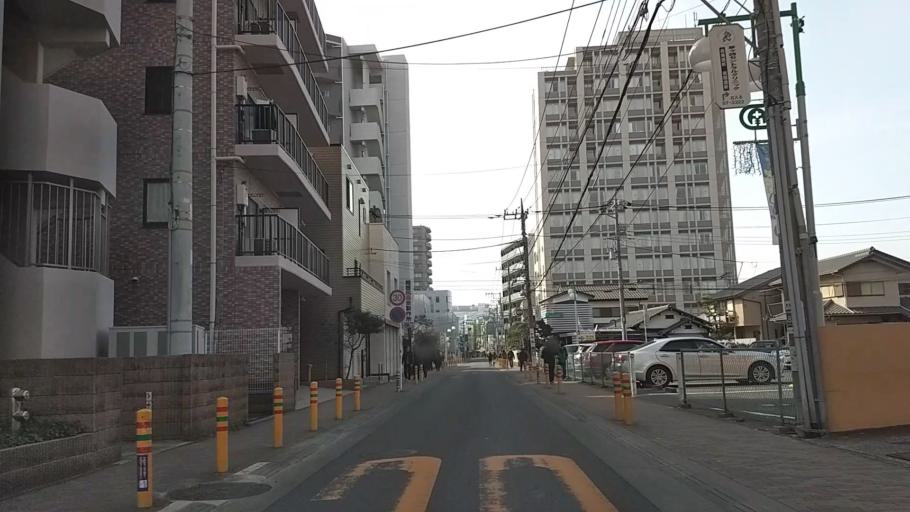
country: JP
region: Kanagawa
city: Chigasaki
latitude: 35.3307
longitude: 139.4112
